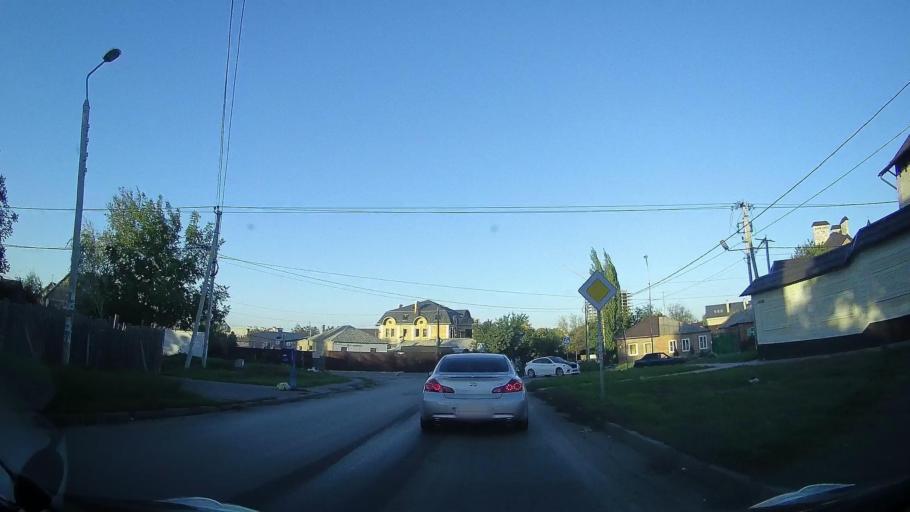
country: RU
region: Rostov
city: Rostov-na-Donu
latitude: 47.2430
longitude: 39.6908
